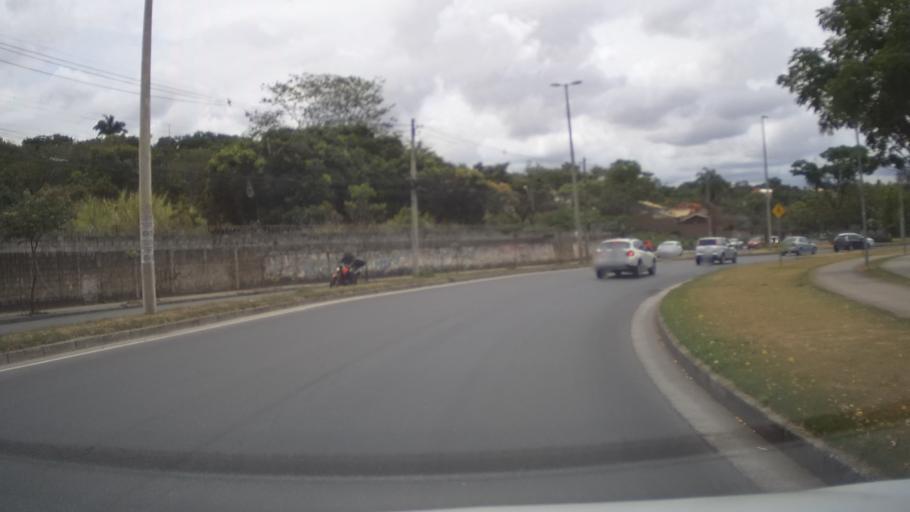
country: BR
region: Minas Gerais
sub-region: Contagem
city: Contagem
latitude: -19.8540
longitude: -44.0060
